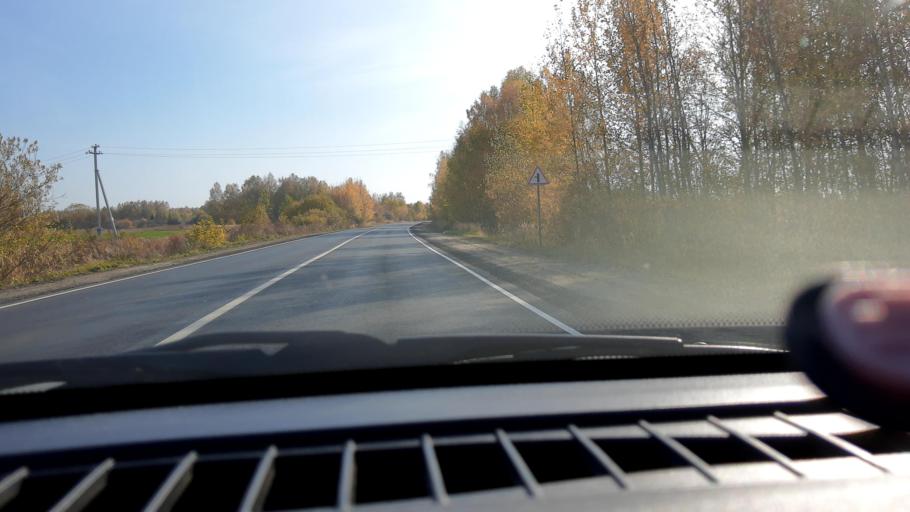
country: RU
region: Nizjnij Novgorod
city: Lukino
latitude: 56.5317
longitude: 43.8037
